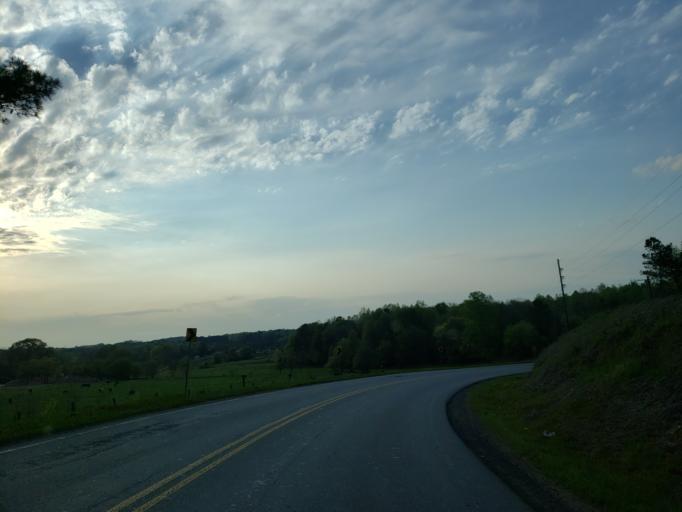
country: US
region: Georgia
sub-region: Cherokee County
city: Ball Ground
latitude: 34.3002
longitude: -84.3998
